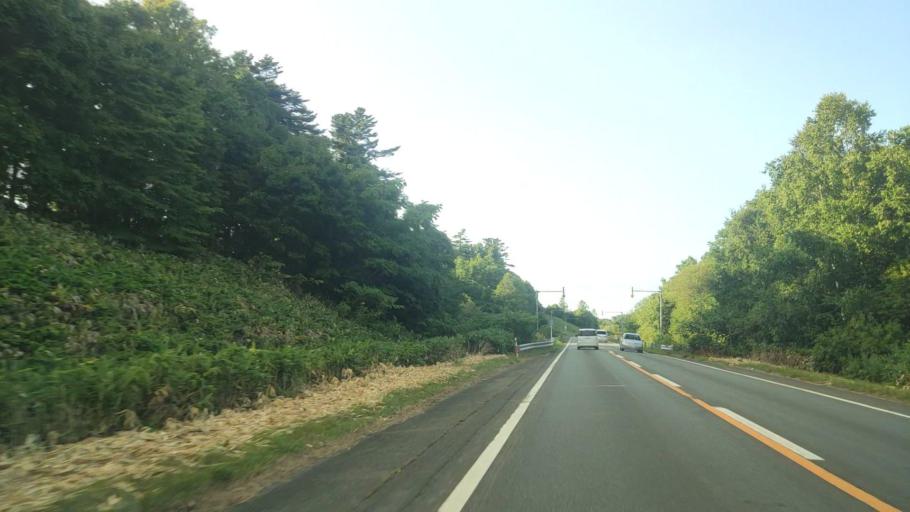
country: JP
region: Hokkaido
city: Makubetsu
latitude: 45.0650
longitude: 141.7482
